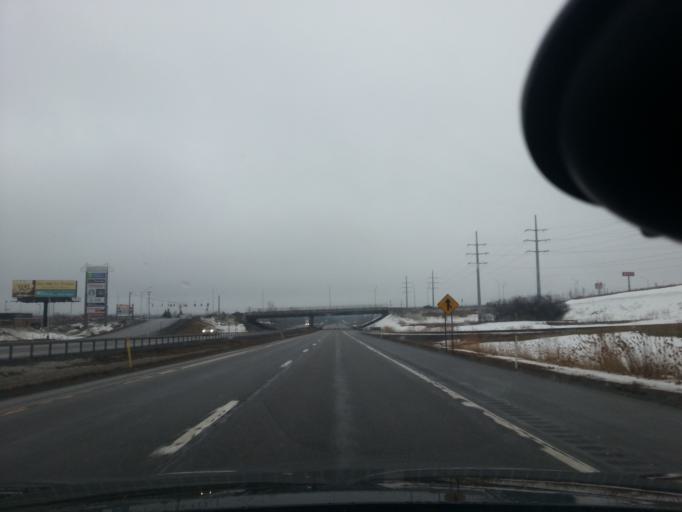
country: US
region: New York
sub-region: Jefferson County
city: Watertown
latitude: 43.9785
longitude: -75.9485
